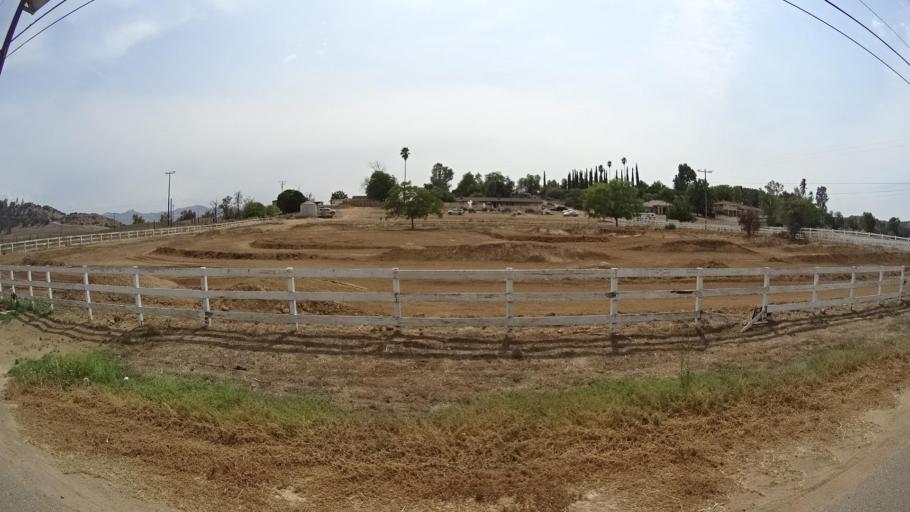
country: US
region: California
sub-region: San Diego County
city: Ramona
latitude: 33.0084
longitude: -116.8922
